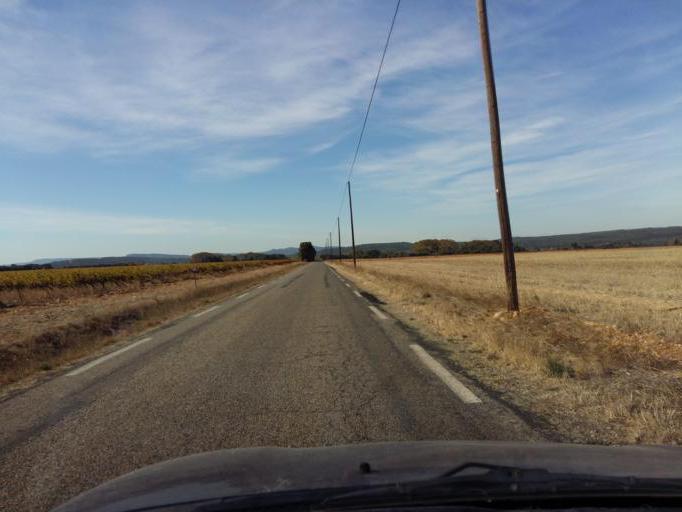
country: FR
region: Provence-Alpes-Cote d'Azur
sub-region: Departement du Vaucluse
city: Serignan-du-Comtat
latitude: 44.1881
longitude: 4.8279
